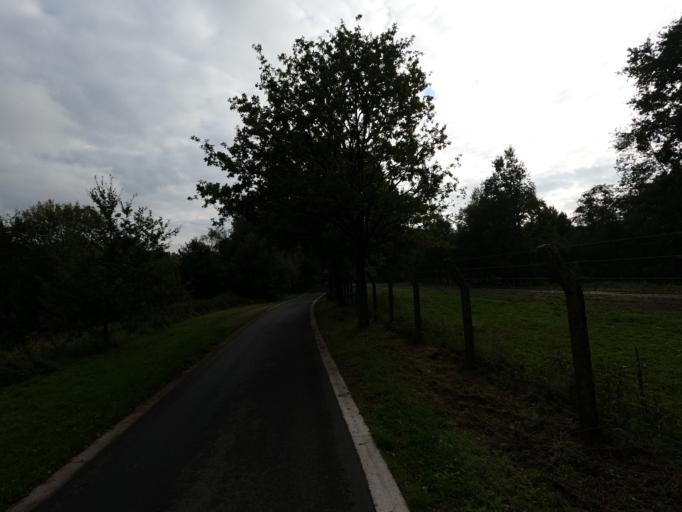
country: BE
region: Flanders
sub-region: Provincie Antwerpen
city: Vorselaar
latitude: 51.1847
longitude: 4.7820
